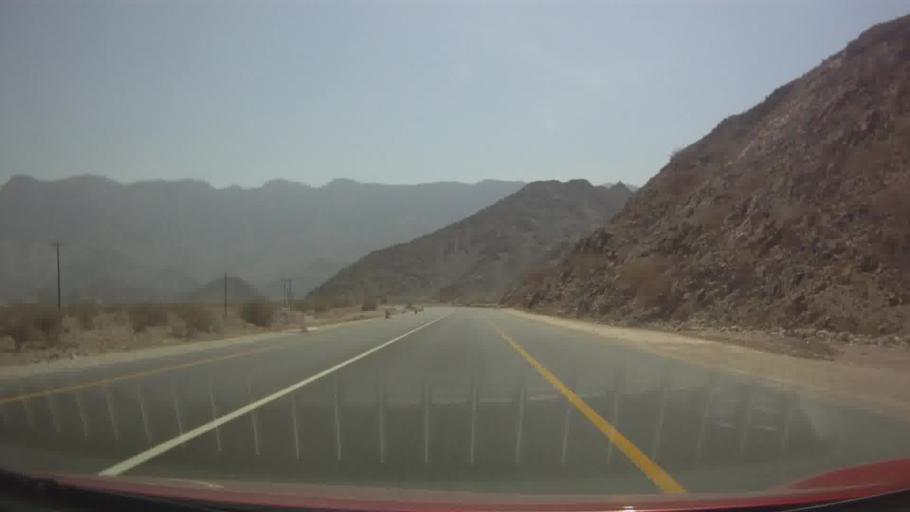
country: OM
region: Muhafazat Masqat
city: Muscat
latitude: 23.4135
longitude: 58.7813
